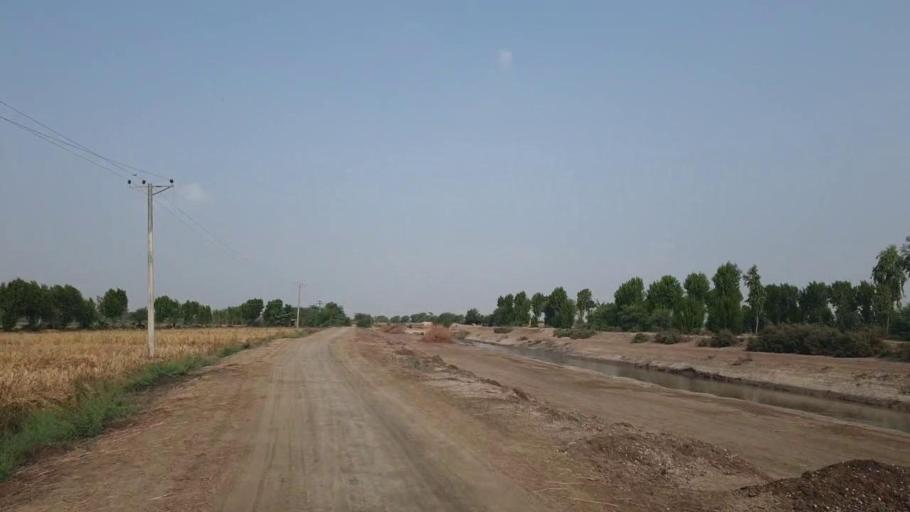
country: PK
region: Sindh
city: Badin
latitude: 24.7517
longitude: 68.7618
